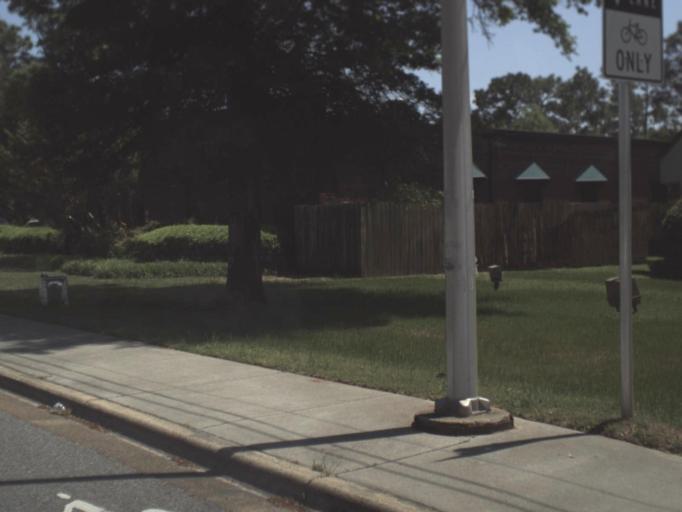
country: US
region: Florida
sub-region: Escambia County
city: Brent
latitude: 30.4767
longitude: -87.2034
